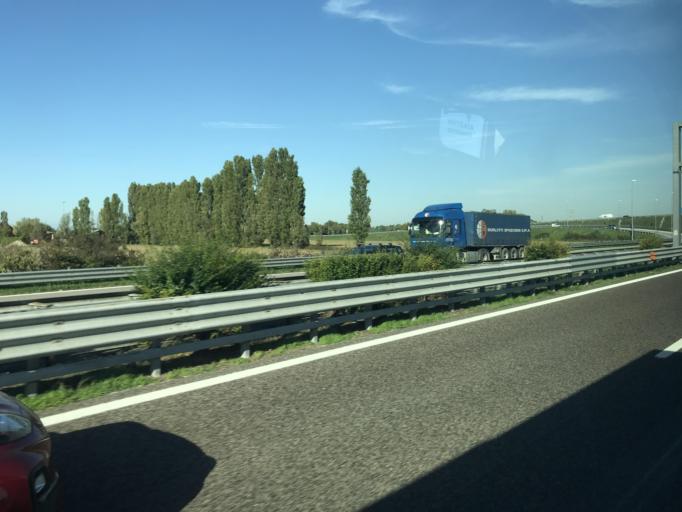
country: IT
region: Veneto
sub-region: Provincia di Venezia
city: Marano
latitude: 45.4534
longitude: 12.1104
